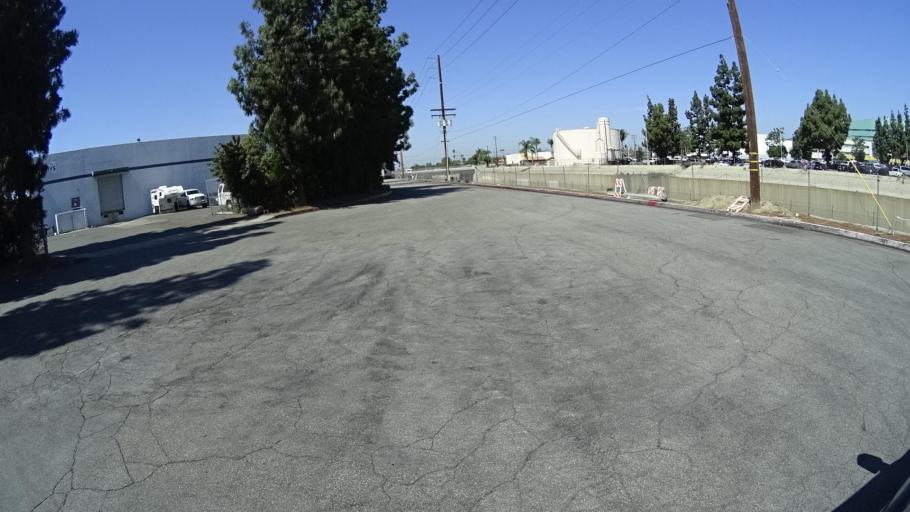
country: US
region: California
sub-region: Los Angeles County
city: West Puente Valley
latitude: 34.0624
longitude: -117.9841
